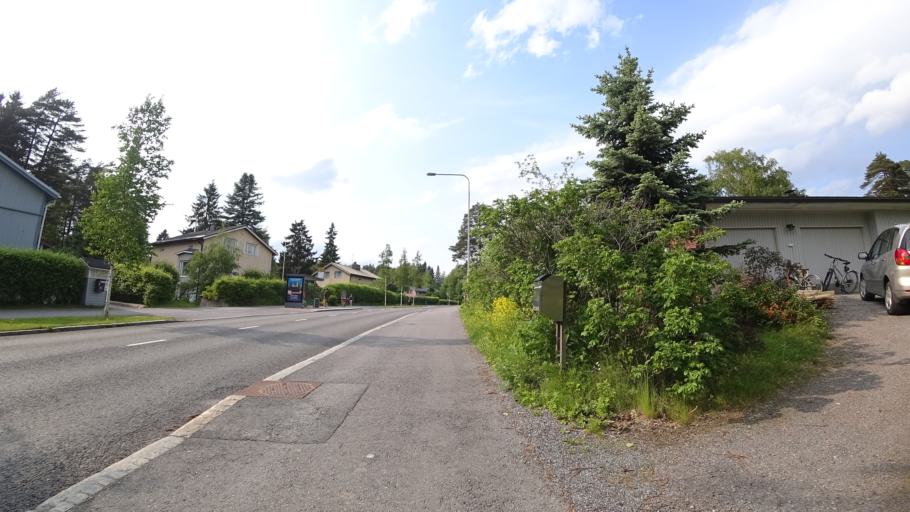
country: FI
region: Pirkanmaa
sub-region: Tampere
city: Pirkkala
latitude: 61.4987
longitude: 23.6295
